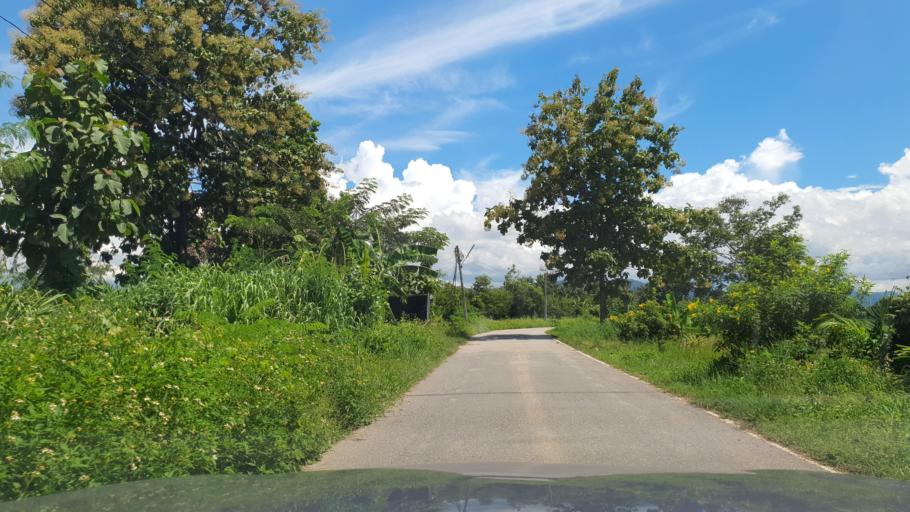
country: TH
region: Chiang Mai
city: San Kamphaeng
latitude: 18.7248
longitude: 99.1356
